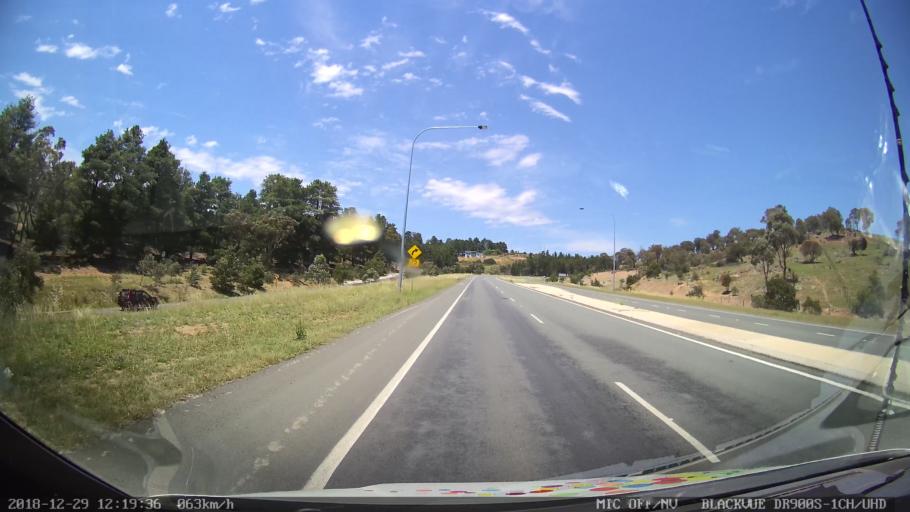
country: AU
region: New South Wales
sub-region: Queanbeyan
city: Queanbeyan
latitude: -35.3953
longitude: 149.2335
